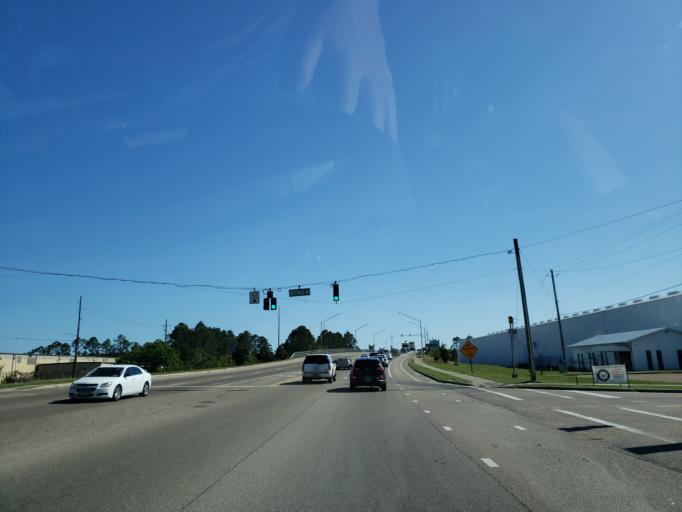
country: US
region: Mississippi
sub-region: Harrison County
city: West Gulfport
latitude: 30.4280
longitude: -89.0313
